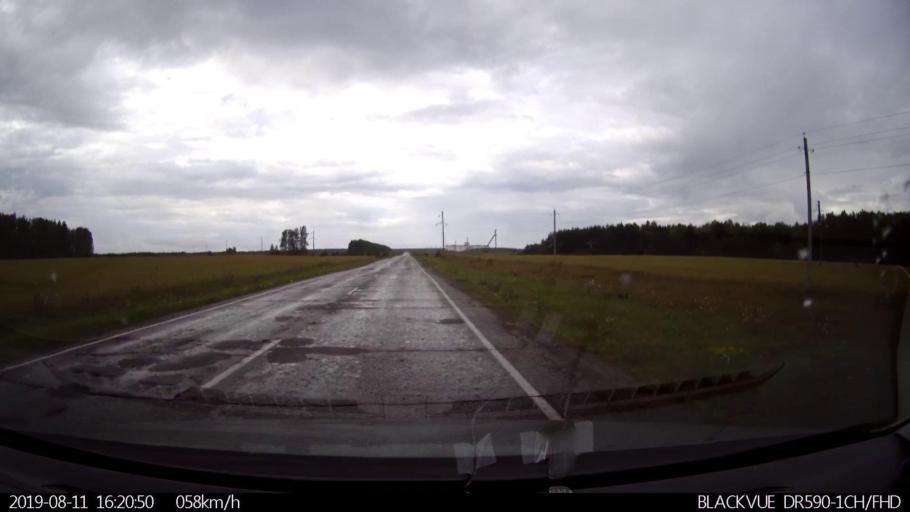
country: RU
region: Ulyanovsk
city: Mayna
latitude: 54.0751
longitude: 47.6009
